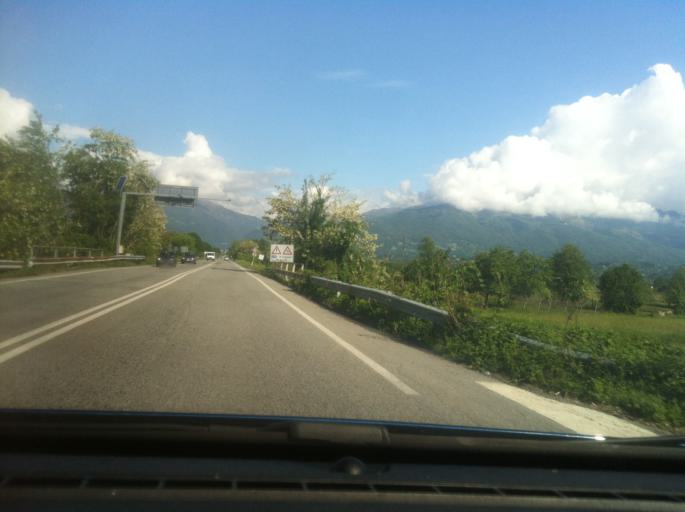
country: IT
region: Piedmont
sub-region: Provincia di Torino
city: Salassa
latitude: 45.3566
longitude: 7.6961
